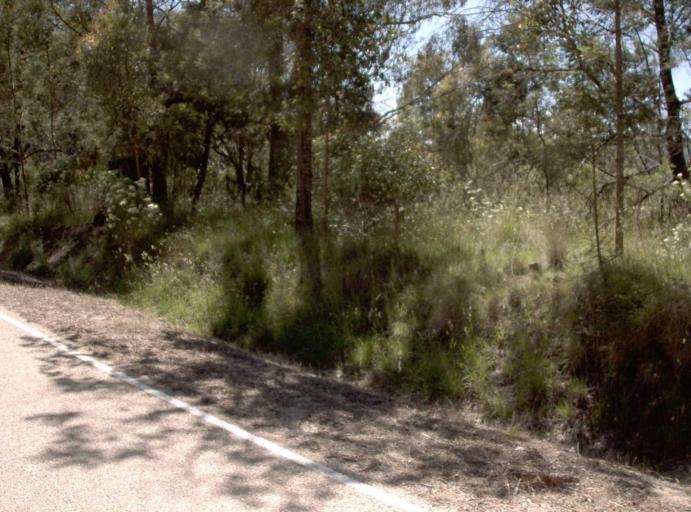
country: AU
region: Victoria
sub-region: East Gippsland
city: Lakes Entrance
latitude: -37.3386
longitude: 148.2292
